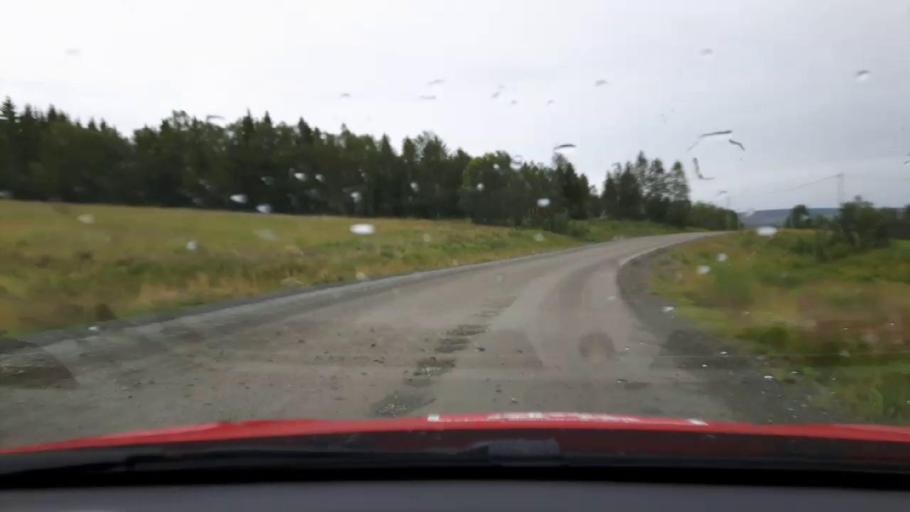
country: SE
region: Jaemtland
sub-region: Are Kommun
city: Are
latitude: 63.4613
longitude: 12.6349
